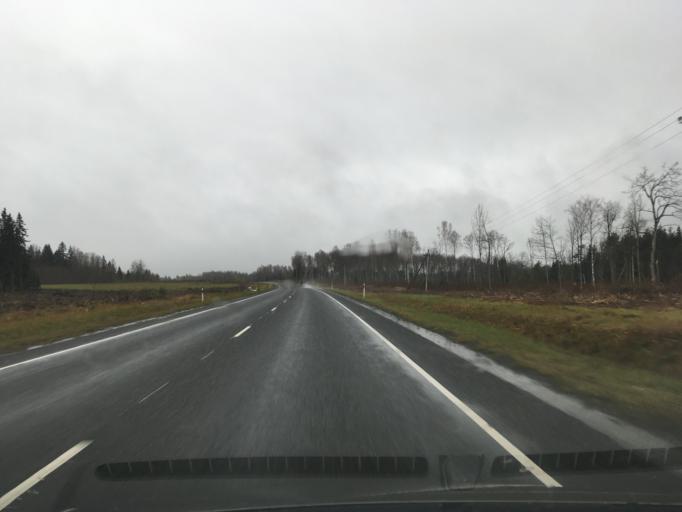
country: EE
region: Harju
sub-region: Nissi vald
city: Turba
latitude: 58.9826
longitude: 24.0576
